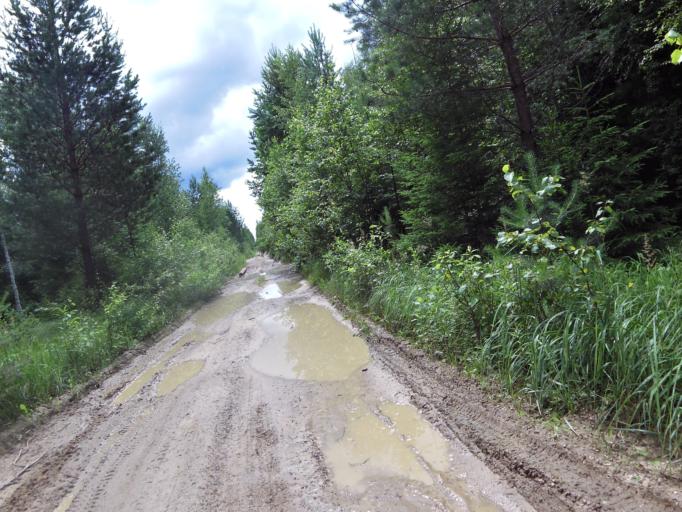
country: RU
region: Moskovskaya
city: Danki
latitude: 54.9335
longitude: 37.6854
